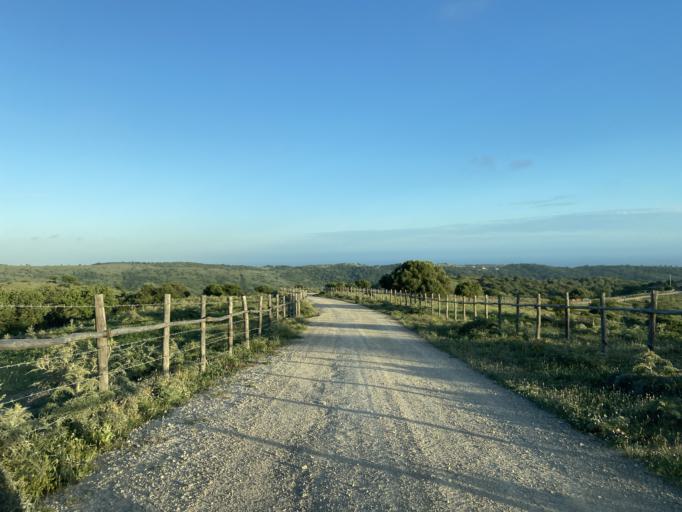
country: IT
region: Latium
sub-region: Citta metropolitana di Roma Capitale
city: Santa Marinella
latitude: 42.0861
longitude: 11.8522
